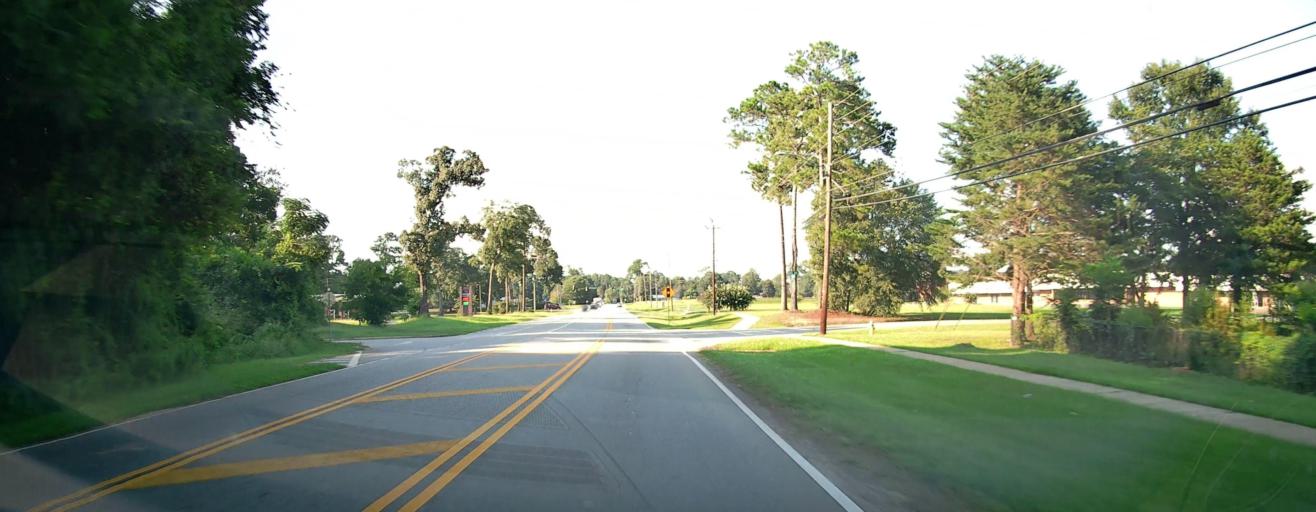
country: US
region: Georgia
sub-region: Houston County
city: Perry
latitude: 32.4664
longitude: -83.7294
